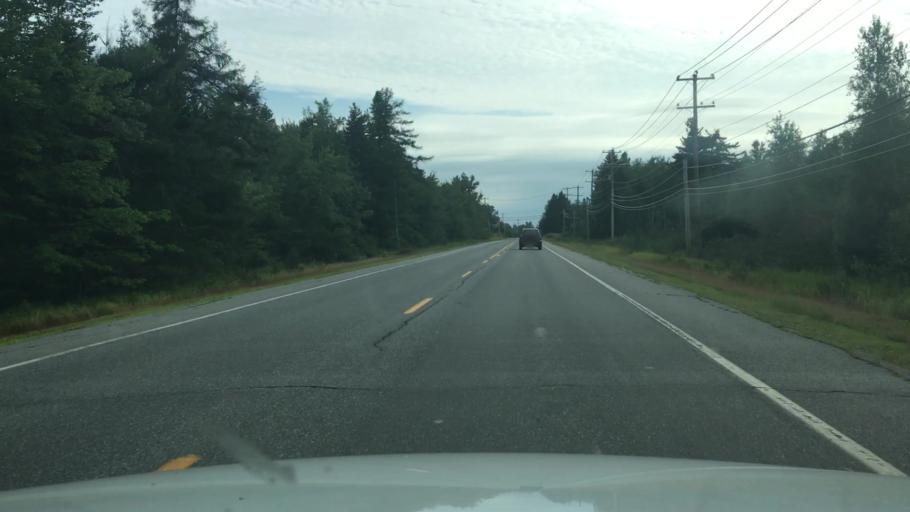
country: US
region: Maine
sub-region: Washington County
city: Addison
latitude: 44.6335
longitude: -67.7756
